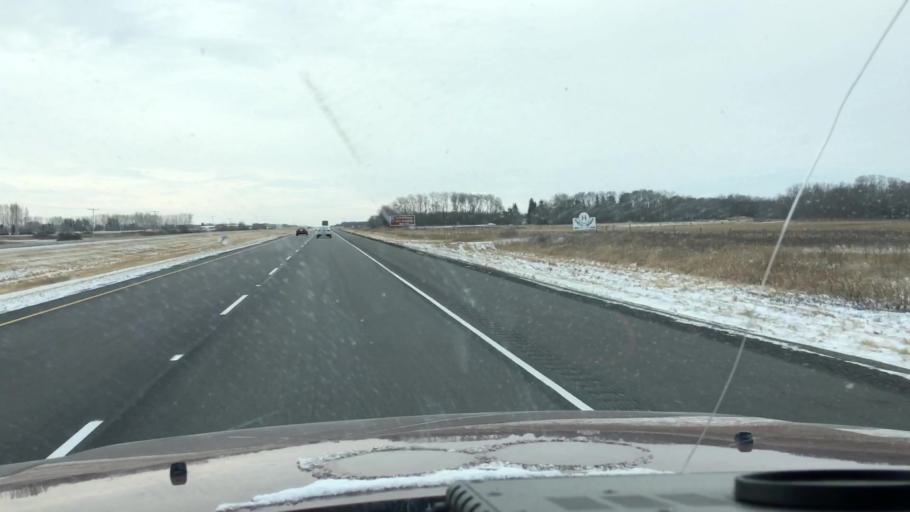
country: CA
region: Saskatchewan
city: Saskatoon
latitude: 51.9788
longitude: -106.5582
